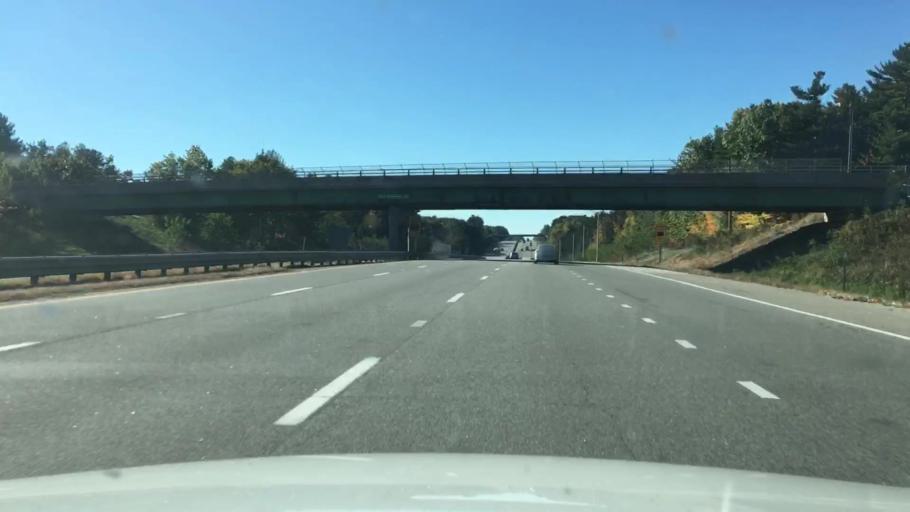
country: US
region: Maine
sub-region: York County
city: West Kennebunk
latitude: 43.4049
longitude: -70.5628
